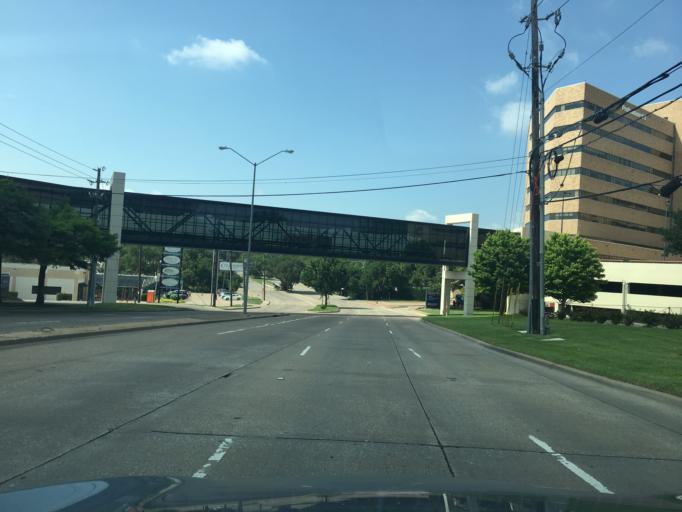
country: US
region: Texas
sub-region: Dallas County
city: University Park
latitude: 32.8832
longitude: -96.7612
